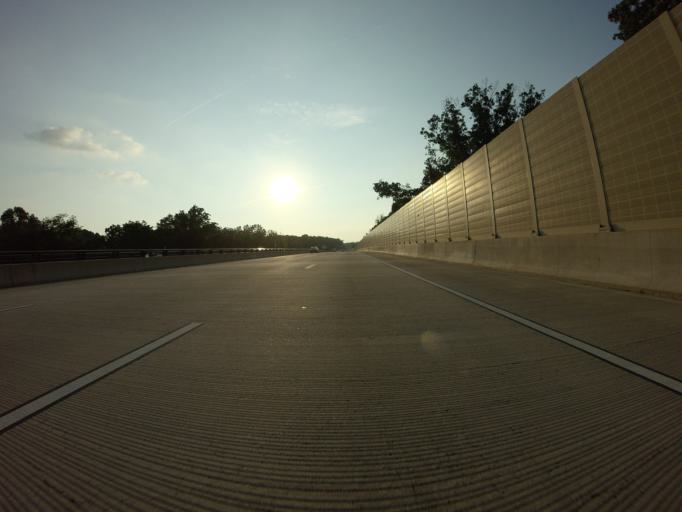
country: US
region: Maryland
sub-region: Montgomery County
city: Fairland
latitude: 39.0844
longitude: -76.9720
